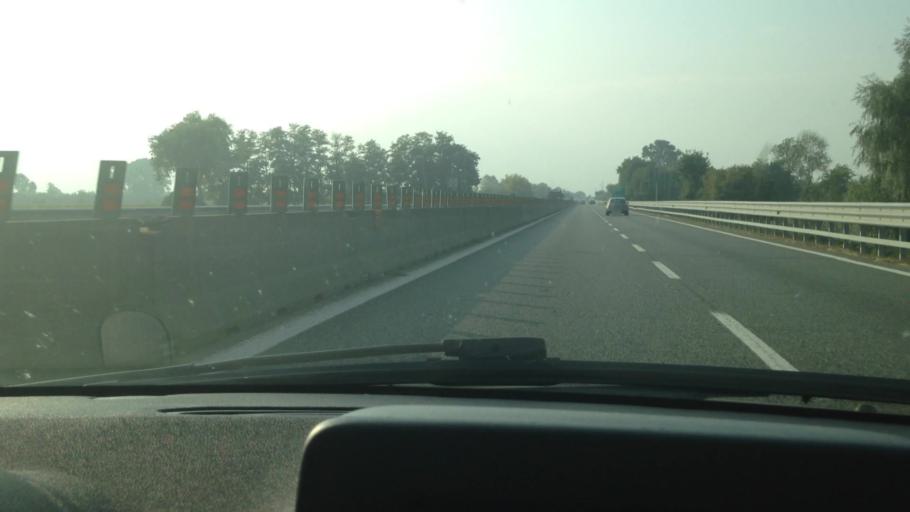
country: IT
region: Piedmont
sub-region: Provincia di Torino
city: Caselle Torinese
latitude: 45.1752
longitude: 7.6666
